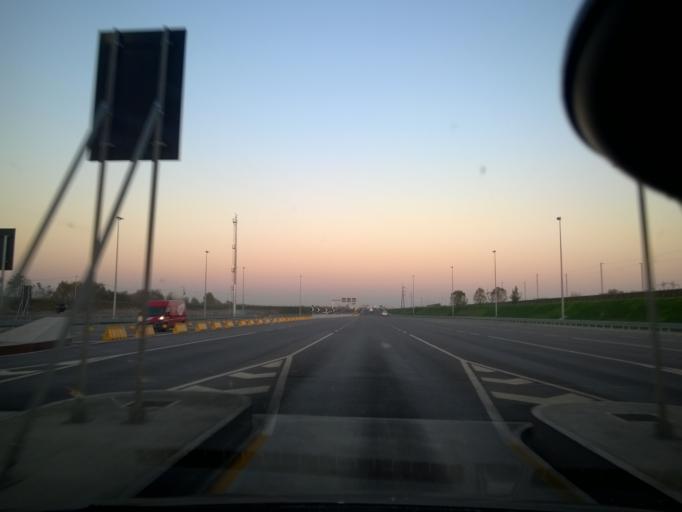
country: IT
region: Lombardy
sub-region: Provincia di Brescia
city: Castrezzato
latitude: 45.5220
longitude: 9.9618
